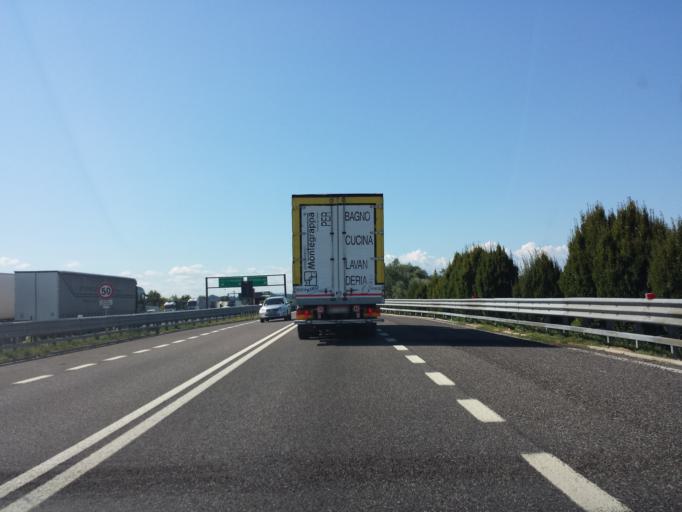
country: IT
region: Veneto
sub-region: Provincia di Vicenza
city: Torri di Quartesolo
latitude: 45.5095
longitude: 11.6096
